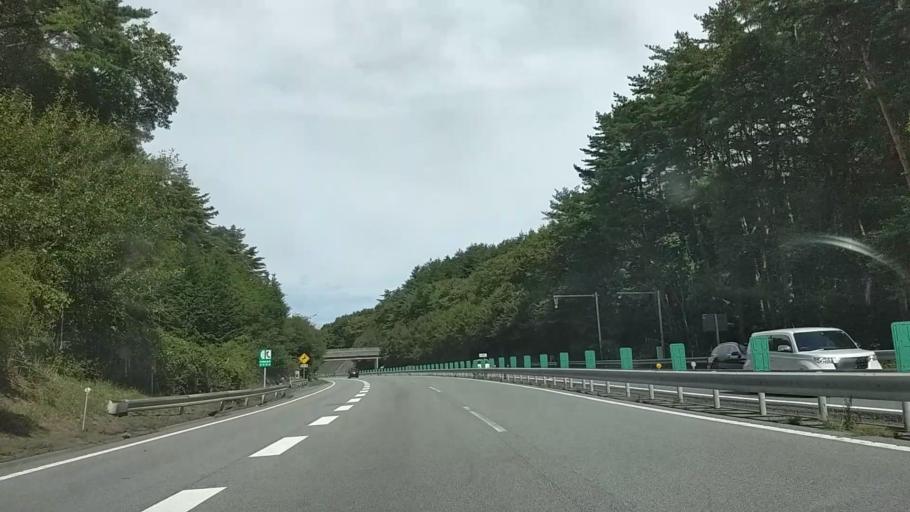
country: JP
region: Yamanashi
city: Nirasaki
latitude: 35.8587
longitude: 138.3319
